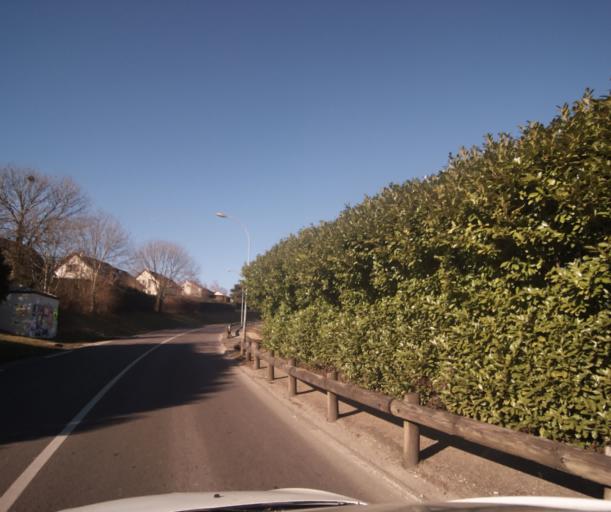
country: FR
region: Franche-Comte
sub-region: Departement du Doubs
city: Avanne-Aveney
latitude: 47.2161
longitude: 5.9597
